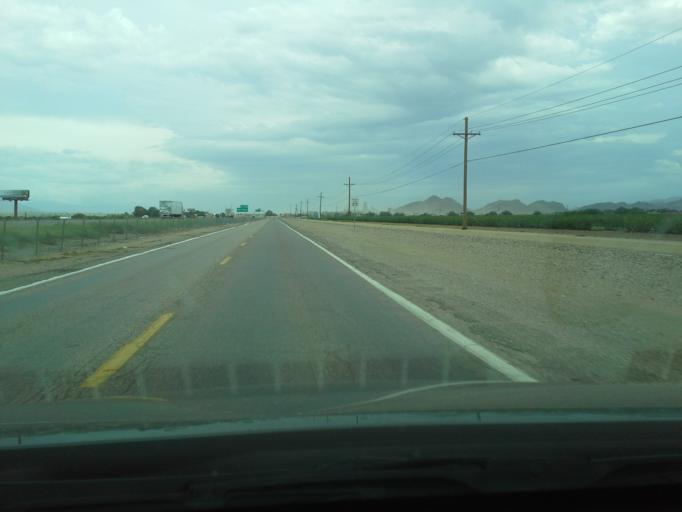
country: US
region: Arizona
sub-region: Pima County
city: Marana
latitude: 32.4313
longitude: -111.1738
